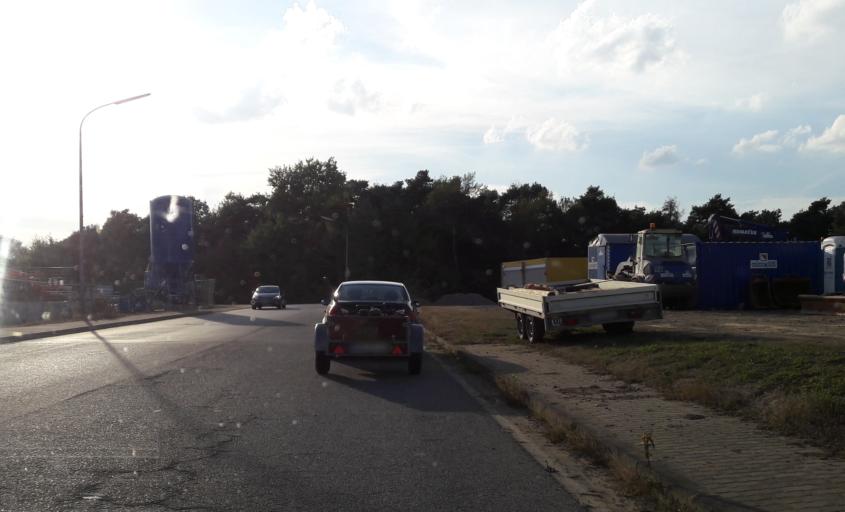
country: DE
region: Rheinland-Pfalz
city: Briedel
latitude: 50.0322
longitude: 7.1567
